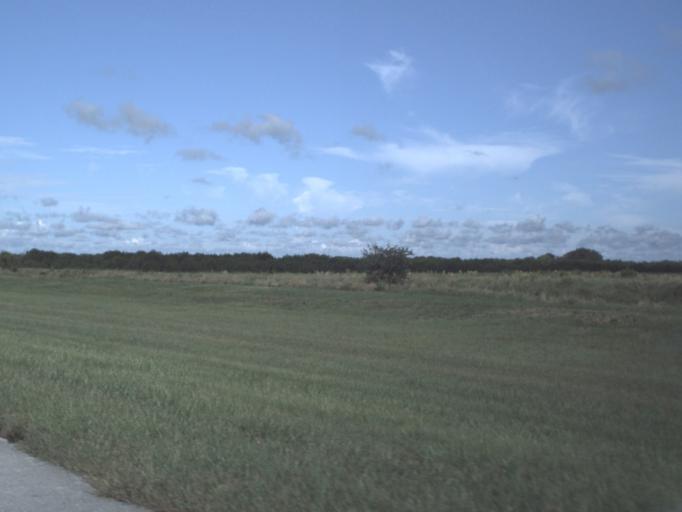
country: US
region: Florida
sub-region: Highlands County
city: Placid Lakes
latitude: 27.2097
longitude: -81.5893
